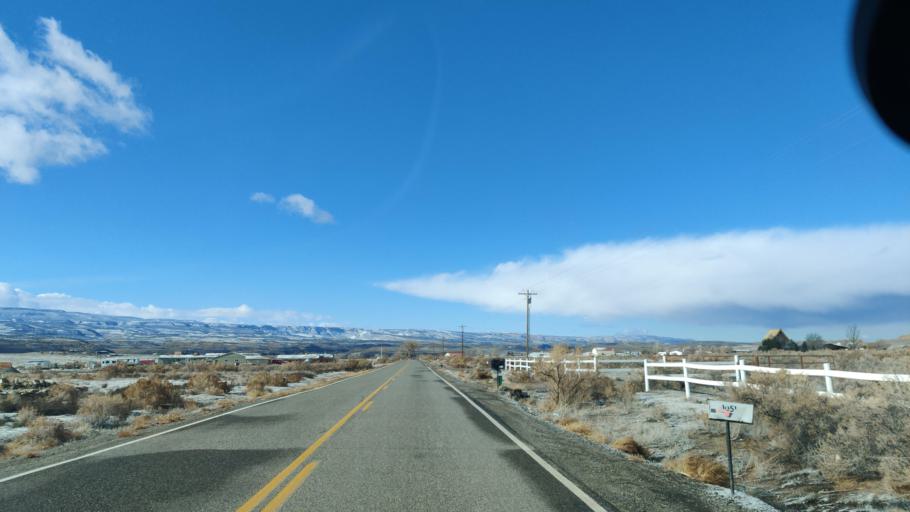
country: US
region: Colorado
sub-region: Mesa County
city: Clifton
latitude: 38.9906
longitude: -108.4307
